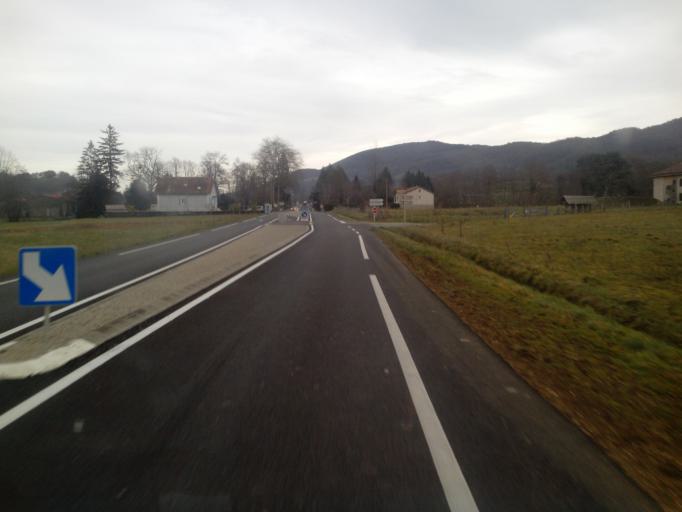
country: FR
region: Midi-Pyrenees
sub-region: Departement de l'Ariege
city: Foix
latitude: 43.0086
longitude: 1.4597
